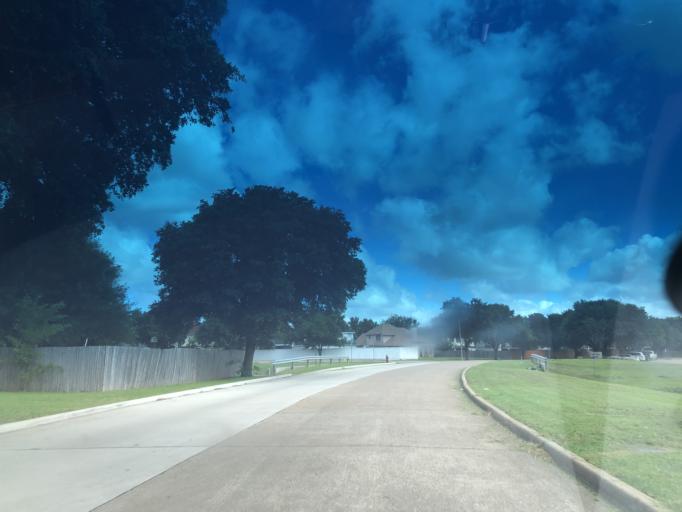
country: US
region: Texas
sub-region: Dallas County
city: Grand Prairie
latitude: 32.6936
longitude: -97.0373
